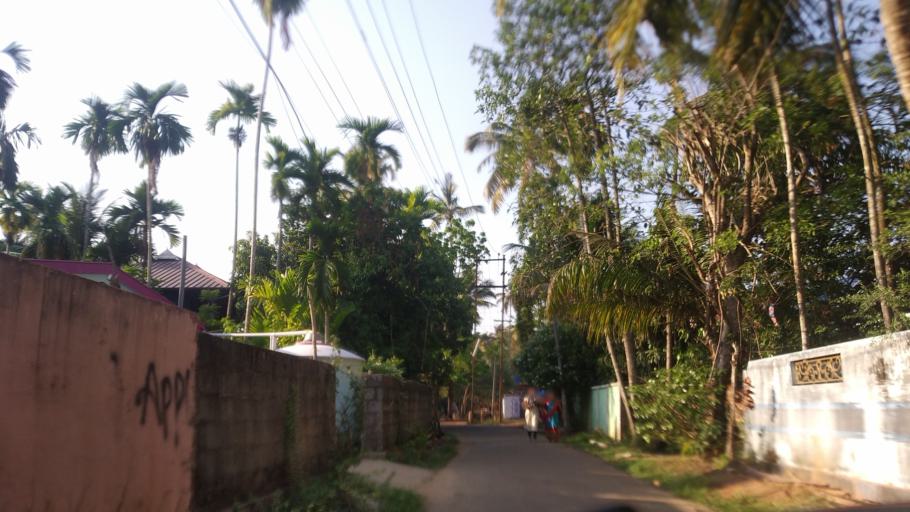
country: IN
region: Kerala
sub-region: Thrissur District
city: Kodungallur
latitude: 10.1384
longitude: 76.2019
